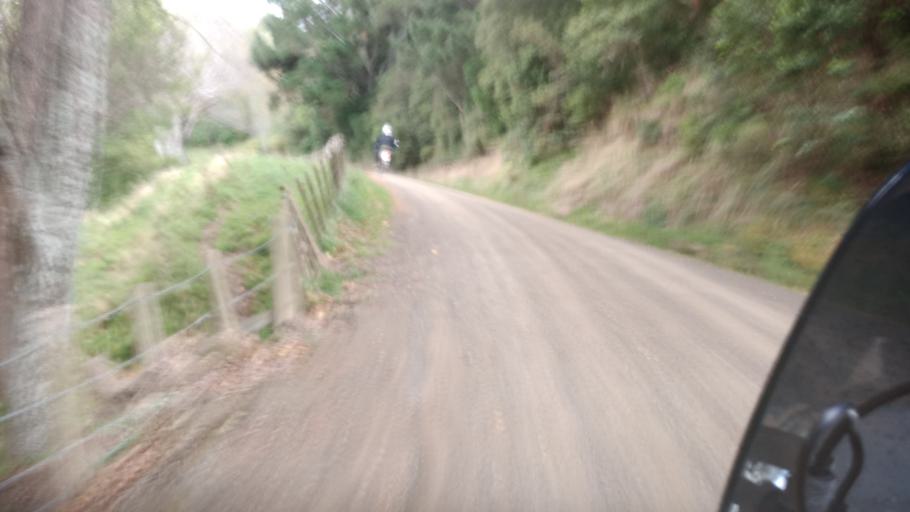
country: NZ
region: Gisborne
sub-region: Gisborne District
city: Gisborne
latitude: -38.4759
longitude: 177.6140
